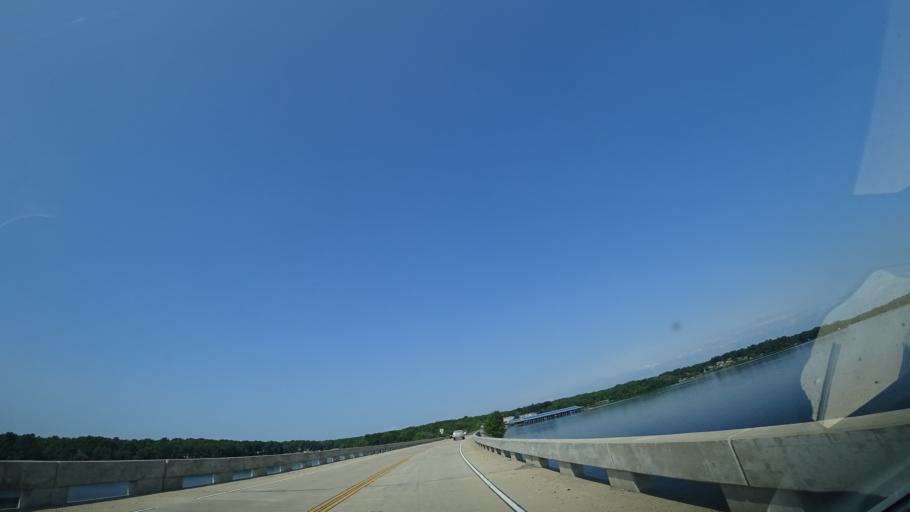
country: US
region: Virginia
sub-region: Louisa County
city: Louisa
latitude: 38.0850
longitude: -77.8140
